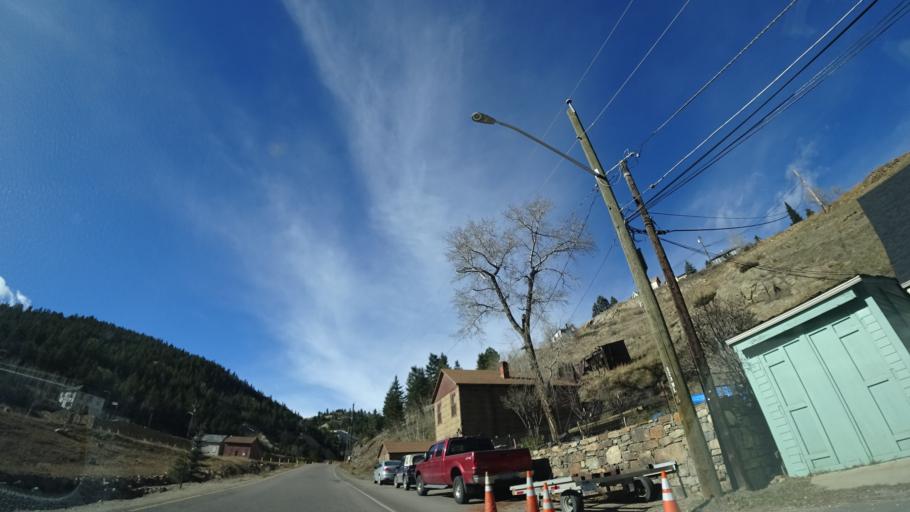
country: US
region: Colorado
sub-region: Gilpin County
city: Central City
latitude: 39.8012
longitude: -105.5042
